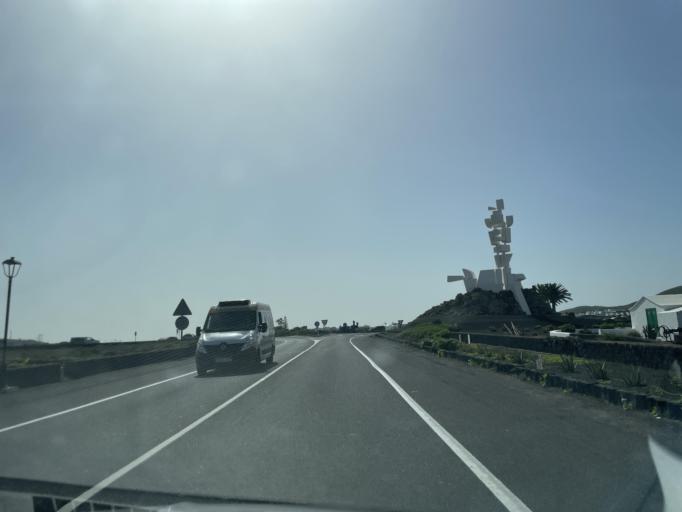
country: ES
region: Canary Islands
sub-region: Provincia de Las Palmas
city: San Bartolome
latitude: 29.0164
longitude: -13.6149
